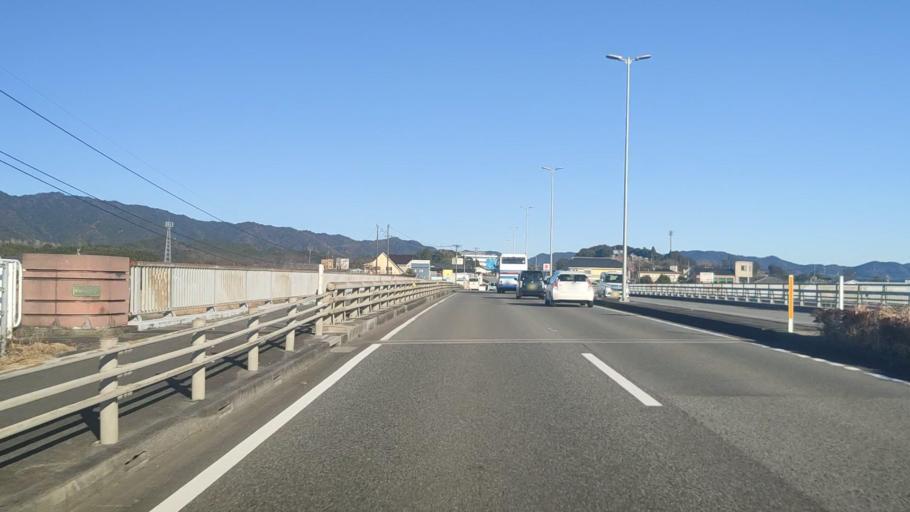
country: JP
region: Miyazaki
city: Nobeoka
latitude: 32.4638
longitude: 131.6487
